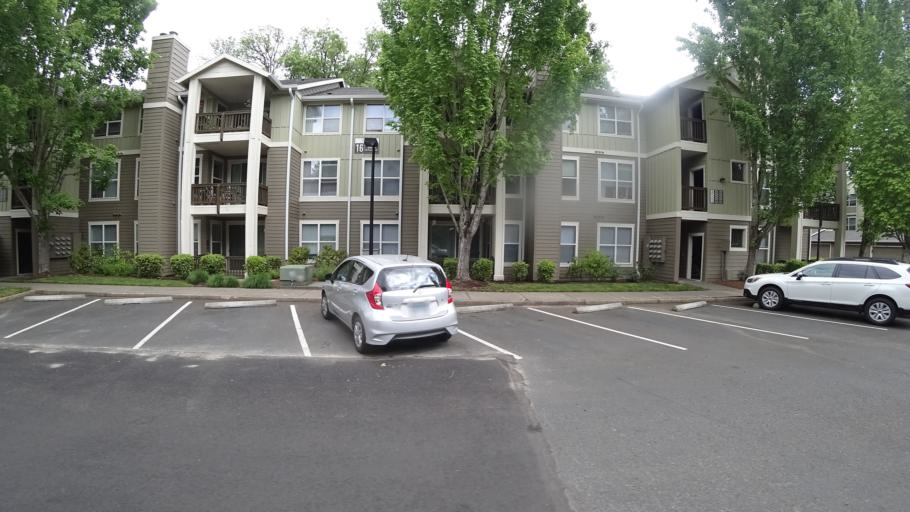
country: US
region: Oregon
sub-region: Washington County
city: Rockcreek
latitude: 45.5364
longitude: -122.8755
